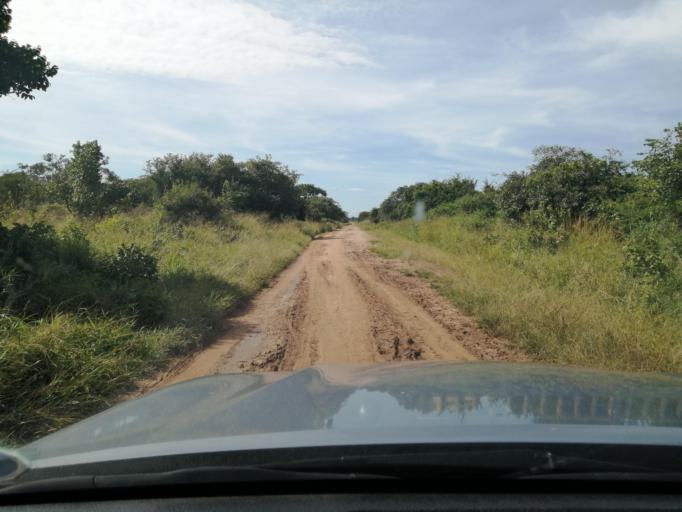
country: ZM
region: Central
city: Chibombo
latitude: -14.9438
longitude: 27.7991
